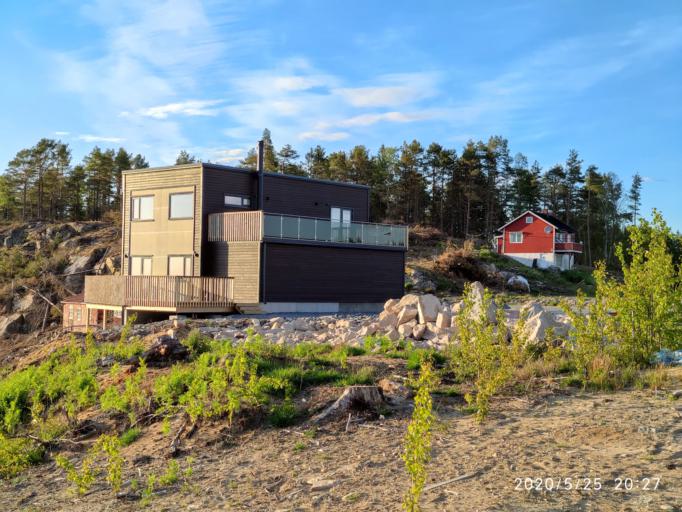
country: NO
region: Ostfold
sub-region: Halden
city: Halden
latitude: 59.1082
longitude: 11.4403
